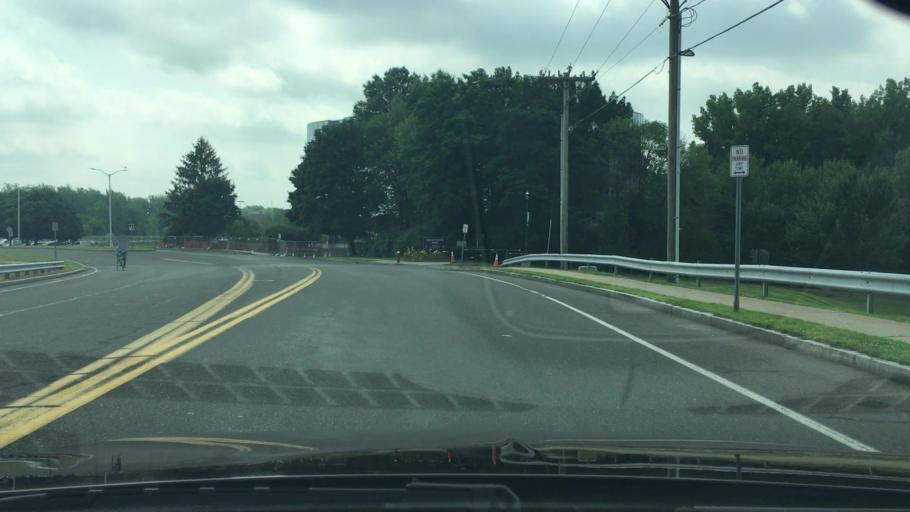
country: US
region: Connecticut
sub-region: Hartford County
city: Hartford
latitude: 41.7599
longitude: -72.6595
